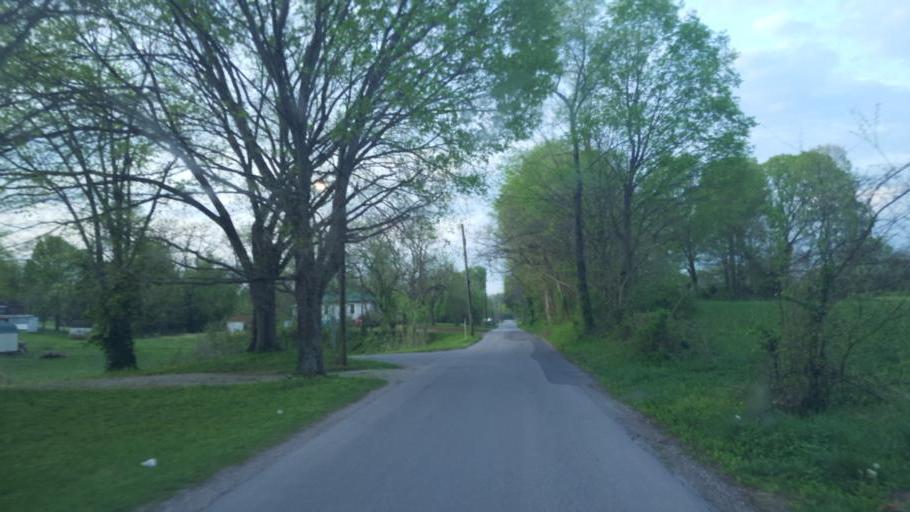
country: US
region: Kentucky
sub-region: Hart County
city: Munfordville
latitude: 37.2804
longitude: -85.9032
